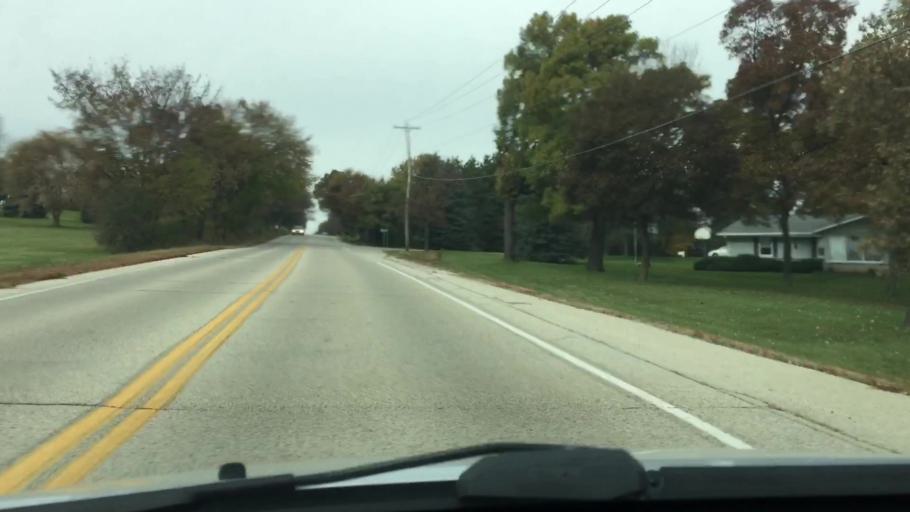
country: US
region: Wisconsin
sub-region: Waukesha County
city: Mukwonago
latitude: 42.8767
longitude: -88.3556
